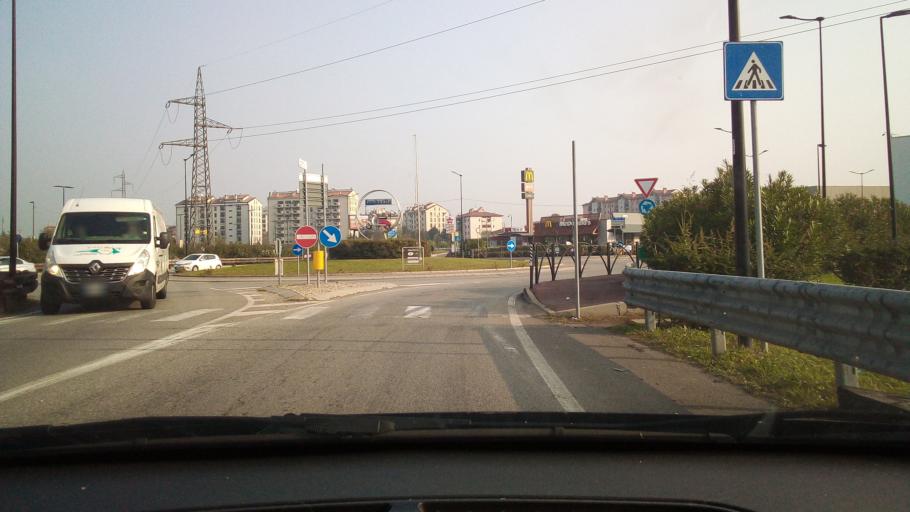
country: IT
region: Lombardy
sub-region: Citta metropolitana di Milano
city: Novegro-Tregarezzo-San Felice
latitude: 45.4854
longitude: 9.2628
